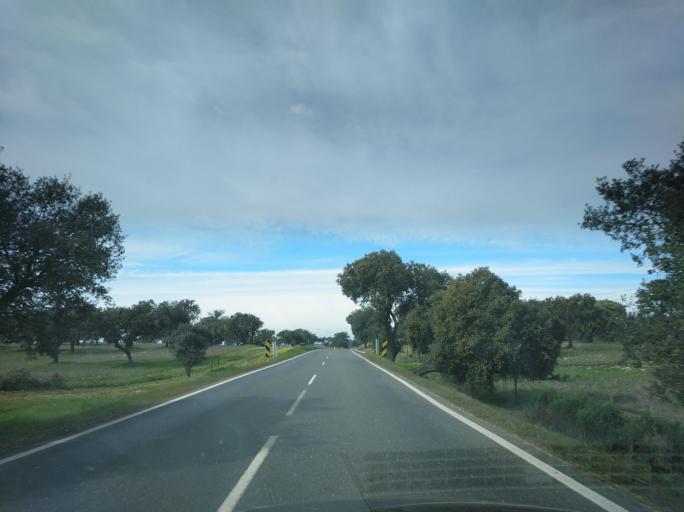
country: PT
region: Beja
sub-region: Mertola
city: Mertola
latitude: 37.7637
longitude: -7.8182
